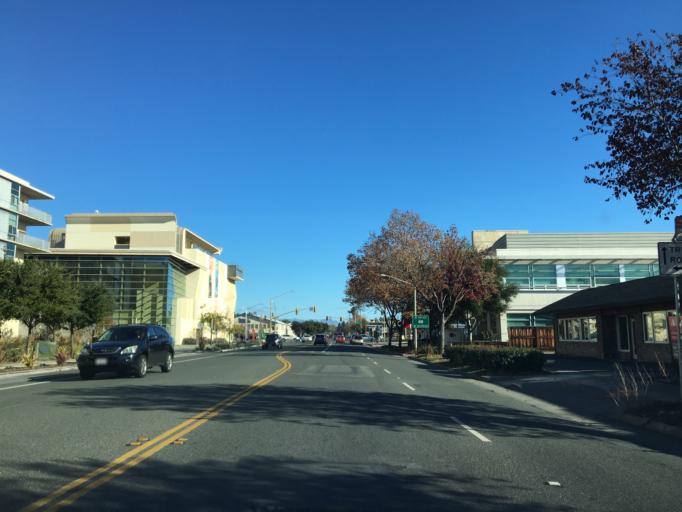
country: US
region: California
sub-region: Santa Clara County
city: Los Altos
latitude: 37.4219
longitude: -122.1034
